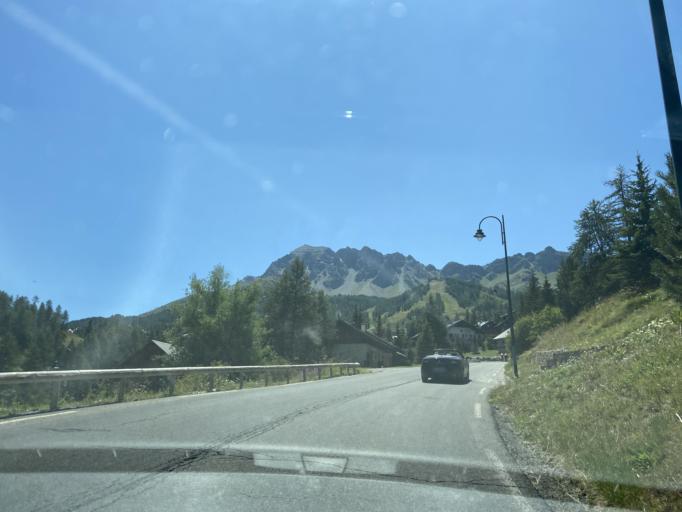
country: FR
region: Provence-Alpes-Cote d'Azur
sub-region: Departement des Hautes-Alpes
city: Guillestre
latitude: 44.5778
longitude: 6.6829
